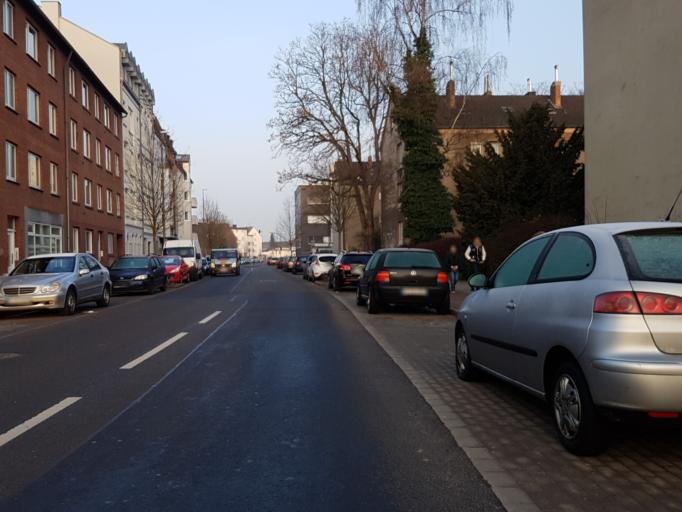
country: DE
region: North Rhine-Westphalia
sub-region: Regierungsbezirk Koln
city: Aachen
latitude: 50.7765
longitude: 6.1191
